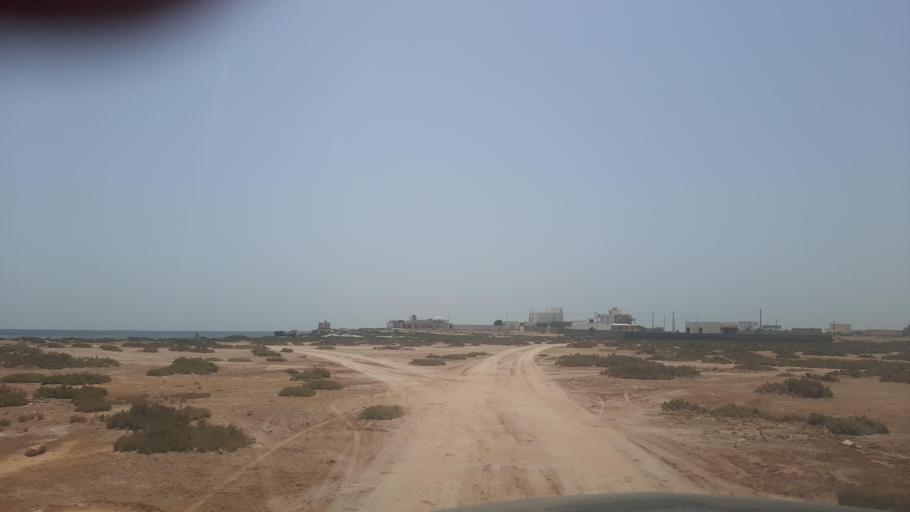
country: TN
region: Al Mahdiyah
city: Mellouleche
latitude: 34.8249
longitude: 11.2599
